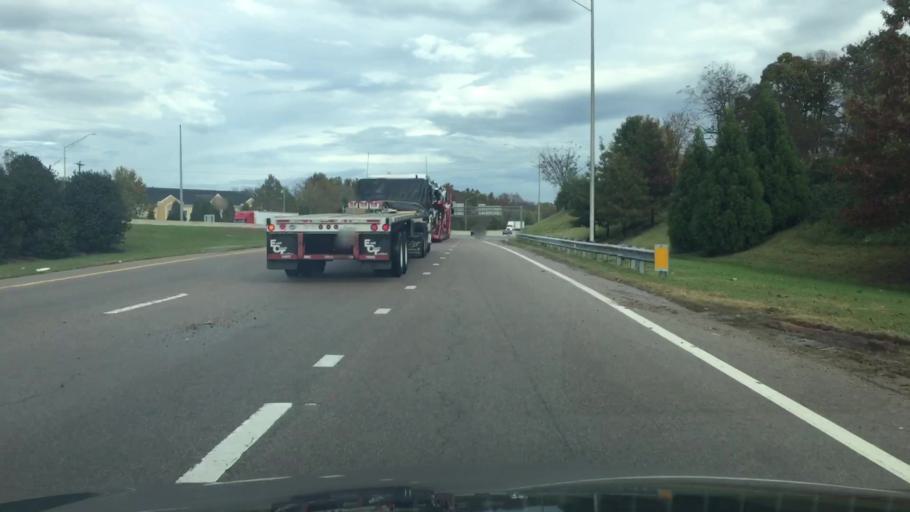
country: US
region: North Carolina
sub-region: Rowan County
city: Salisbury
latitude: 35.6580
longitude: -80.4576
